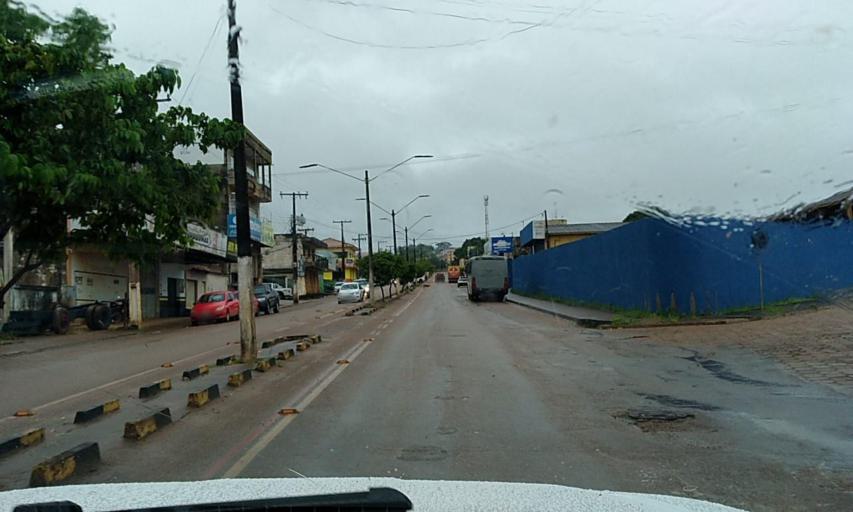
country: BR
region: Para
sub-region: Altamira
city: Altamira
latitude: -3.2123
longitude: -52.2287
